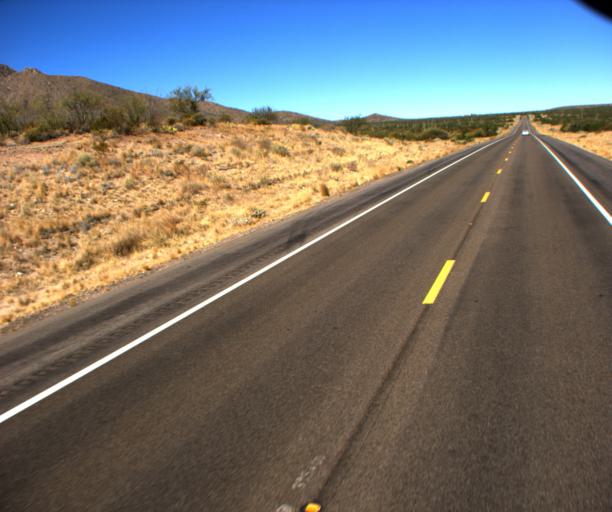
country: US
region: Arizona
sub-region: Pima County
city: Three Points
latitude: 32.0371
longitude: -111.5229
